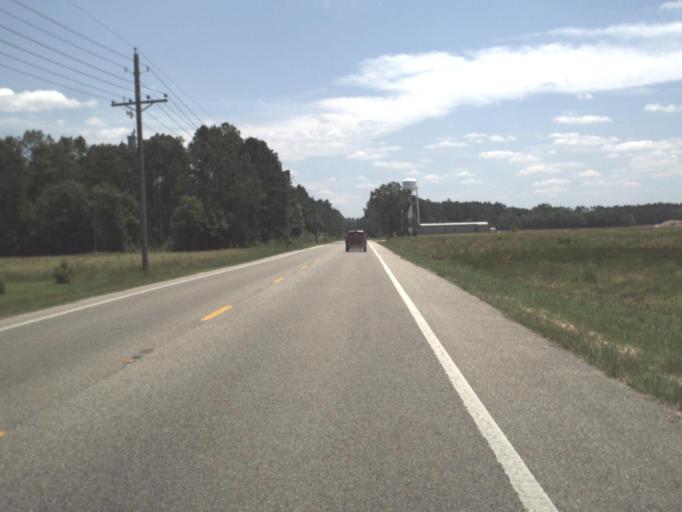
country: US
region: Florida
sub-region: Calhoun County
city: Blountstown
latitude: 30.4930
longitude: -85.1109
